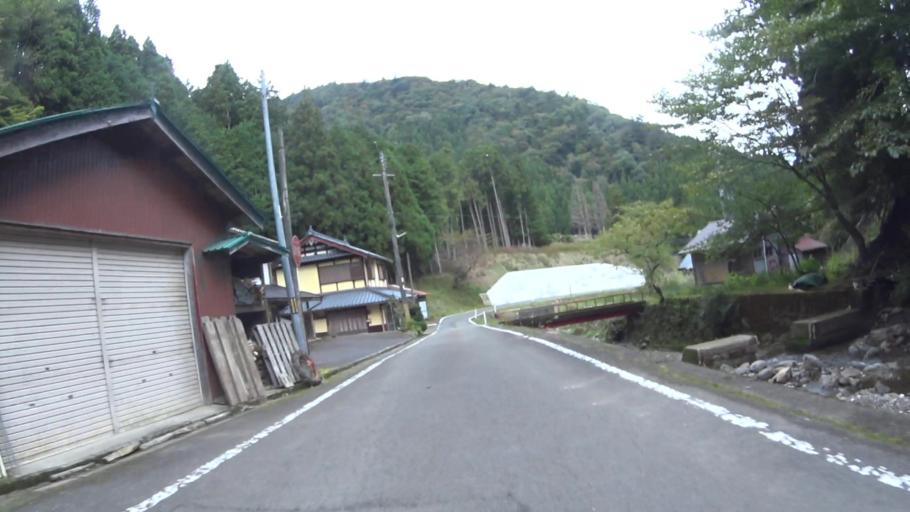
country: JP
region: Fukui
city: Obama
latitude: 35.2799
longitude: 135.6956
